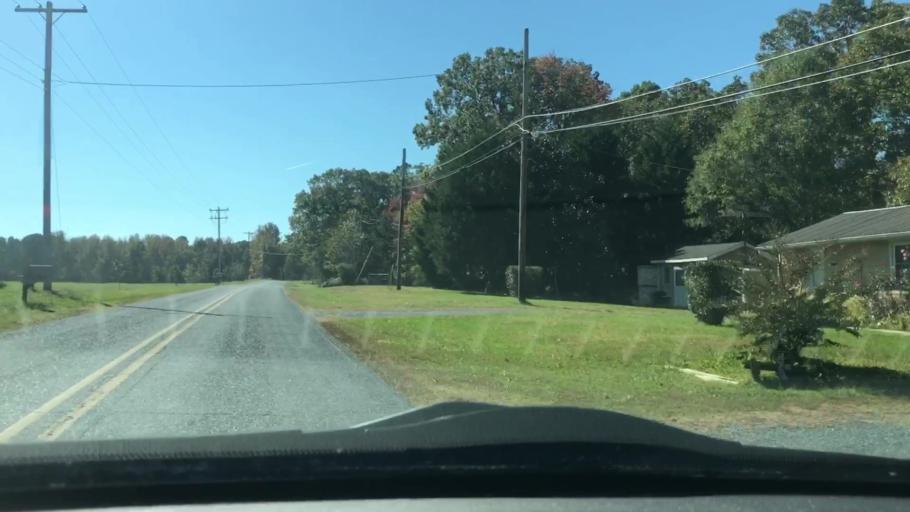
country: US
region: North Carolina
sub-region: Randolph County
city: Randleman
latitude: 35.8132
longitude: -79.8205
